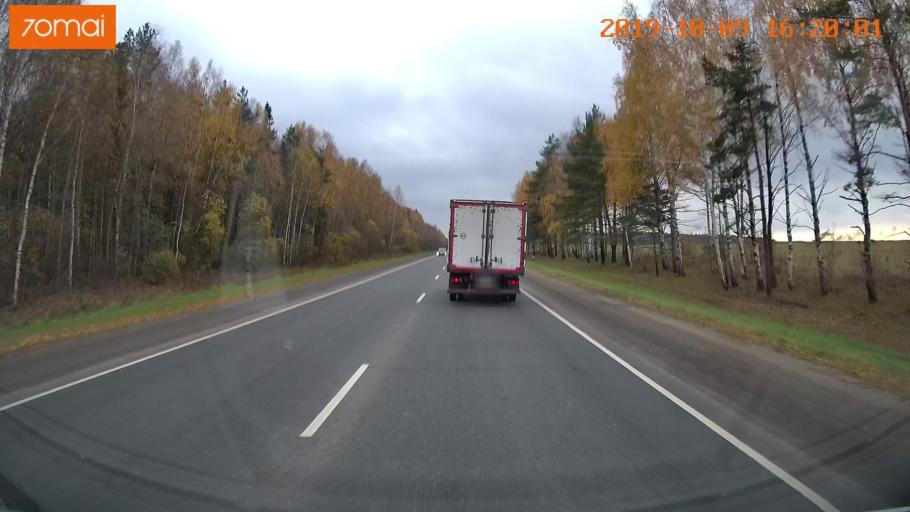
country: RU
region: Kostroma
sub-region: Kostromskoy Rayon
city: Kostroma
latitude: 57.7119
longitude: 40.8933
